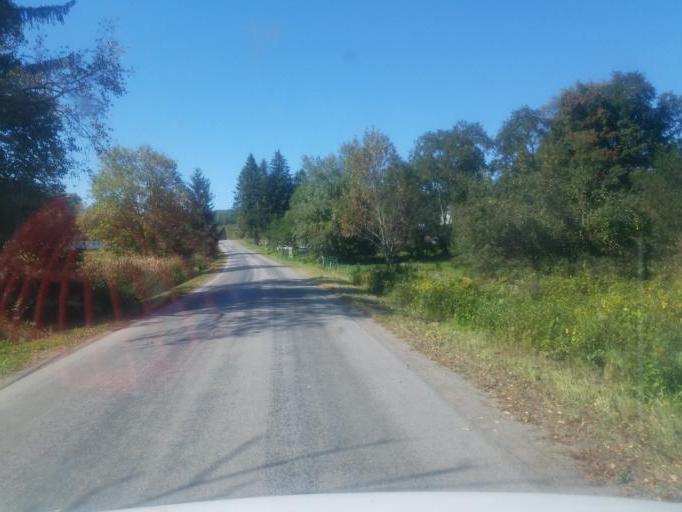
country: US
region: New York
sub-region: Allegany County
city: Friendship
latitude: 42.3008
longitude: -78.1926
